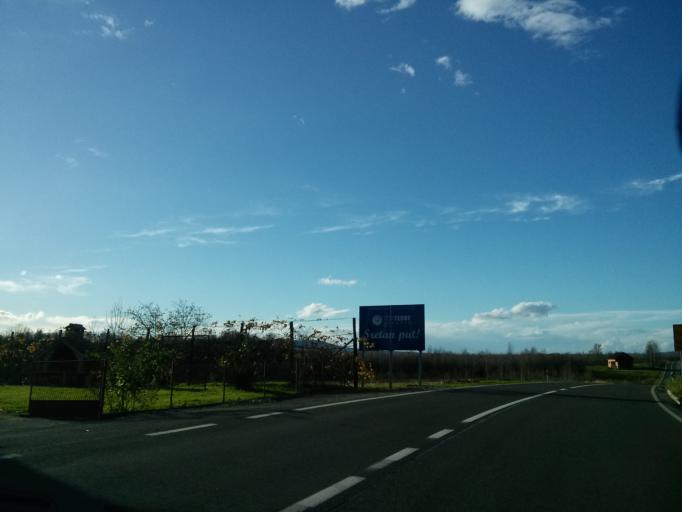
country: HR
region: Sisacko-Moslavacka
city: Gvozd
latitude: 45.3197
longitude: 15.9533
